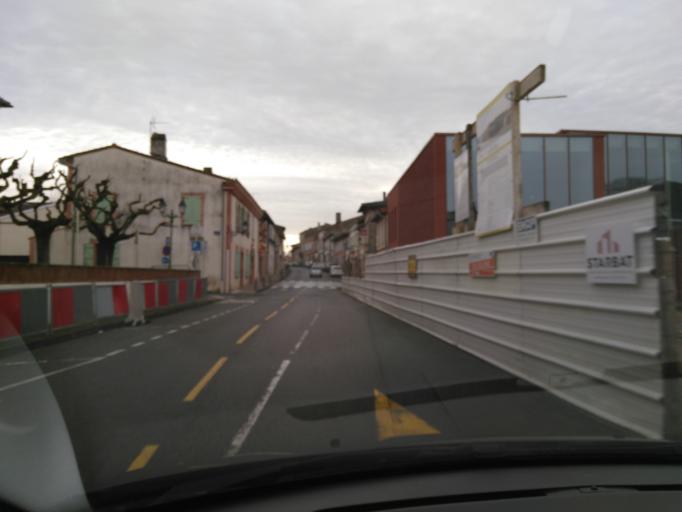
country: FR
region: Midi-Pyrenees
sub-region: Departement de la Haute-Garonne
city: Castelnau-d'Estretefonds
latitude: 43.7837
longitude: 1.3574
